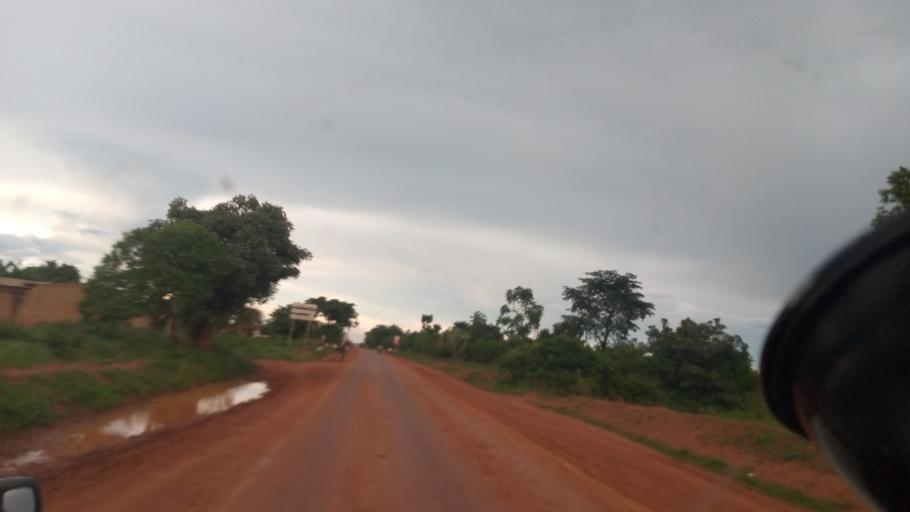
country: UG
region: Northern Region
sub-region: Kole District
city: Kole
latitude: 2.4755
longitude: 32.9361
